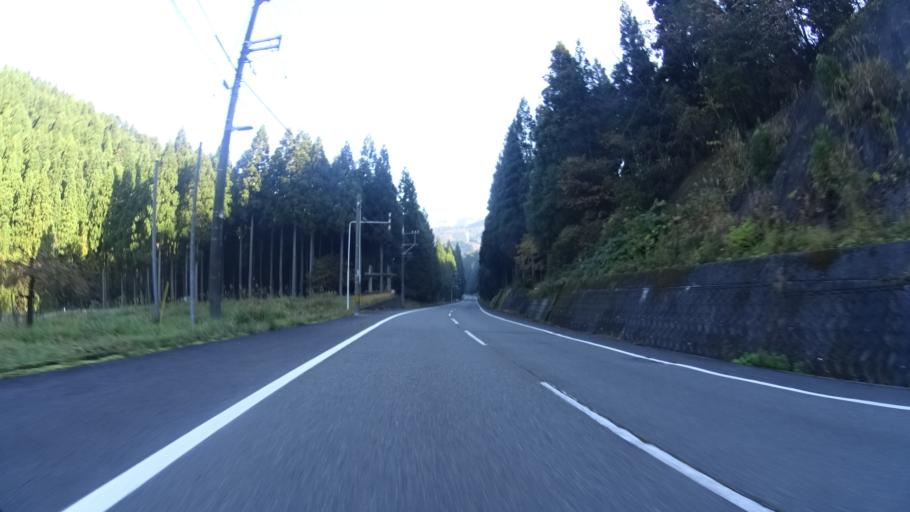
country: JP
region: Fukui
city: Maruoka
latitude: 36.1491
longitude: 136.3284
